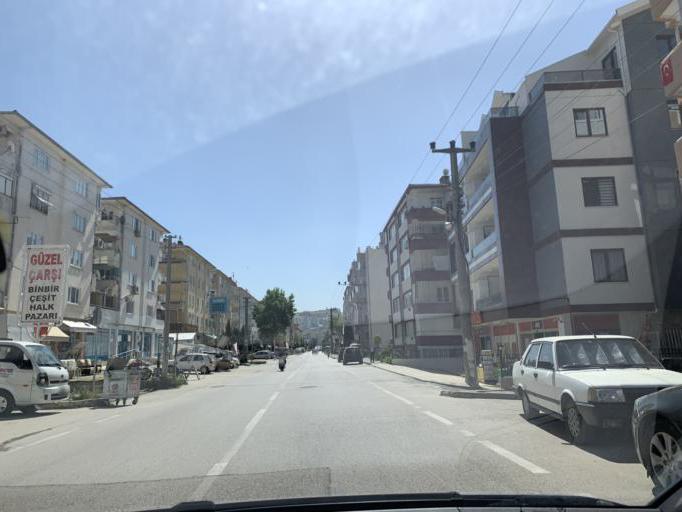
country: TR
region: Bursa
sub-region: Mudanya
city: Mudanya
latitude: 40.3573
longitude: 28.9181
